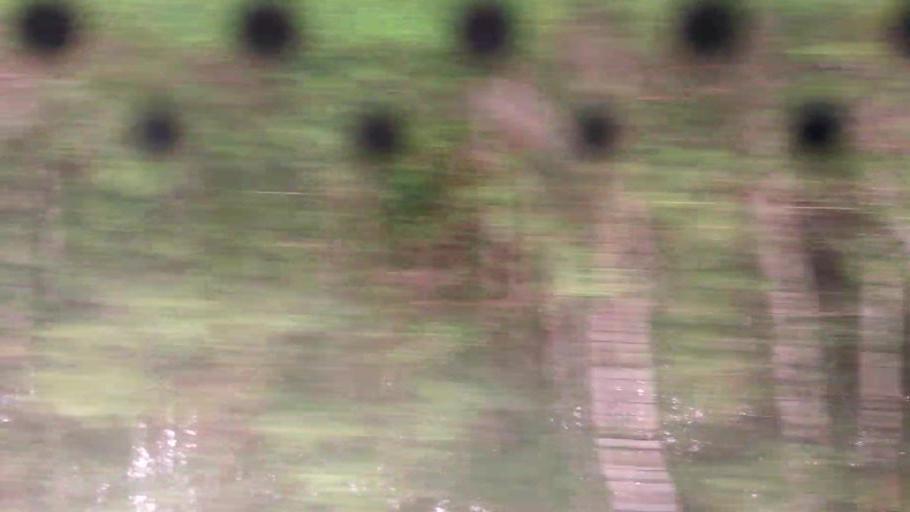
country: RU
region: Moskovskaya
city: Kolomna
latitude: 55.0539
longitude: 38.8680
